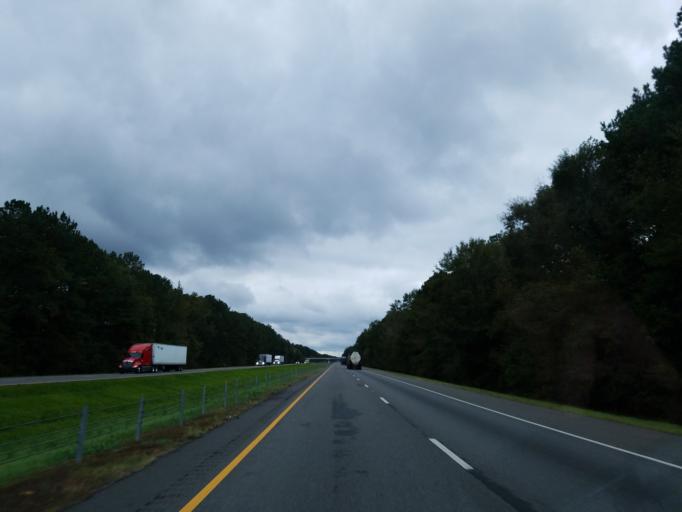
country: US
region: Alabama
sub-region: Greene County
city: Eutaw
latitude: 32.7662
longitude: -88.0658
